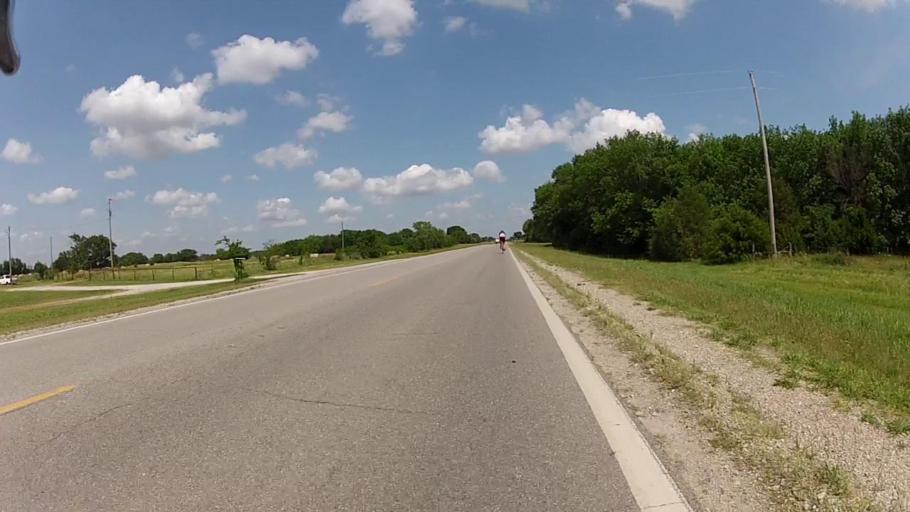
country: US
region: Kansas
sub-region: Labette County
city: Altamont
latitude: 37.1930
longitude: -95.2761
